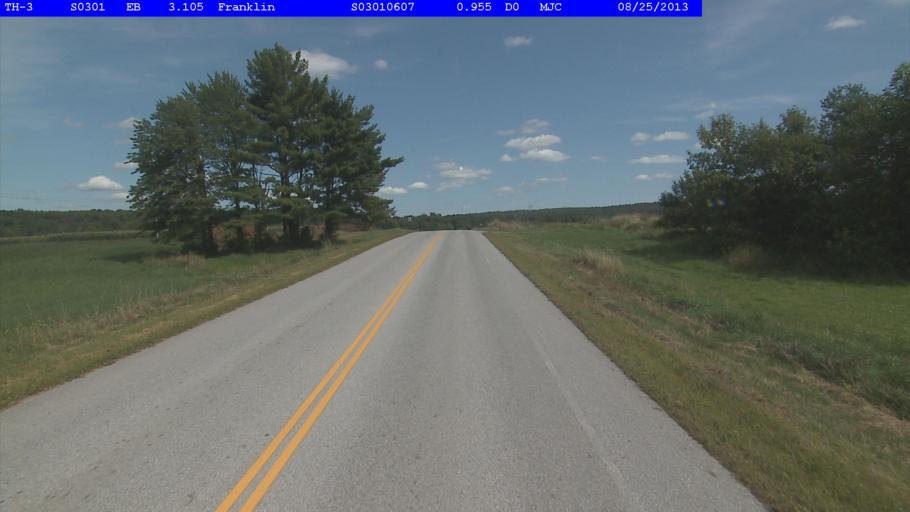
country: CA
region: Quebec
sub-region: Monteregie
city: Bedford
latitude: 44.9686
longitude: -72.9634
